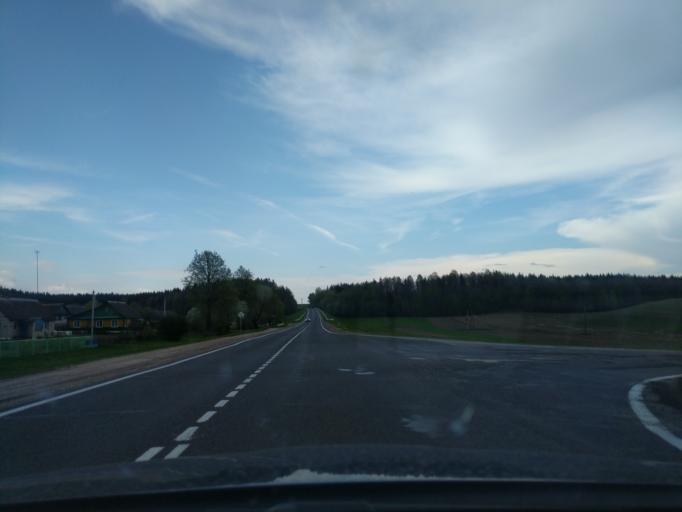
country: BY
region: Grodnenskaya
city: Navahrudak
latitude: 53.6234
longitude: 25.8907
